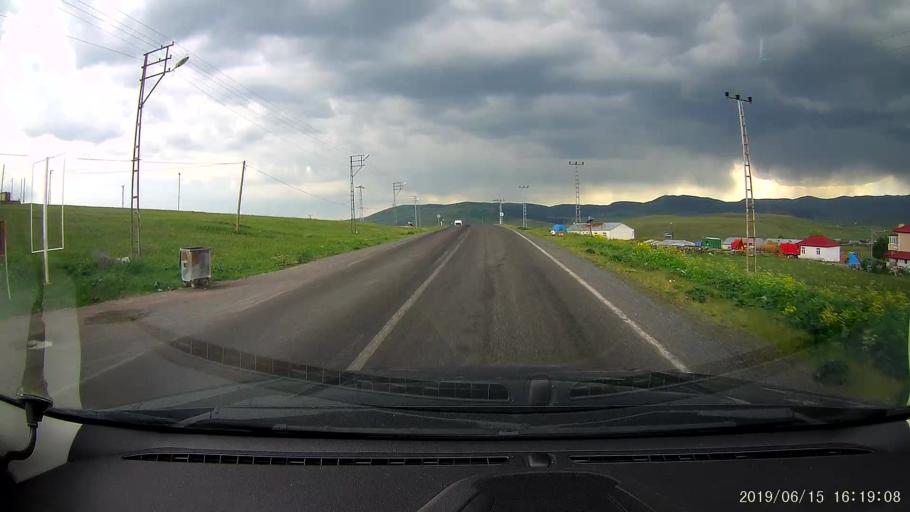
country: TR
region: Ardahan
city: Hanak
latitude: 41.2318
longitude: 42.8521
